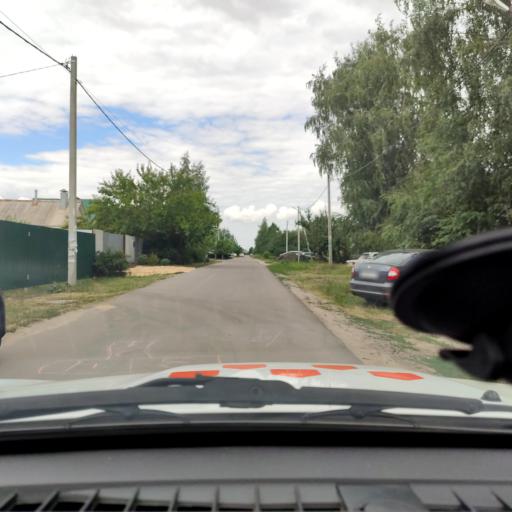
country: RU
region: Voronezj
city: Ramon'
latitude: 51.8268
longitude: 39.2581
